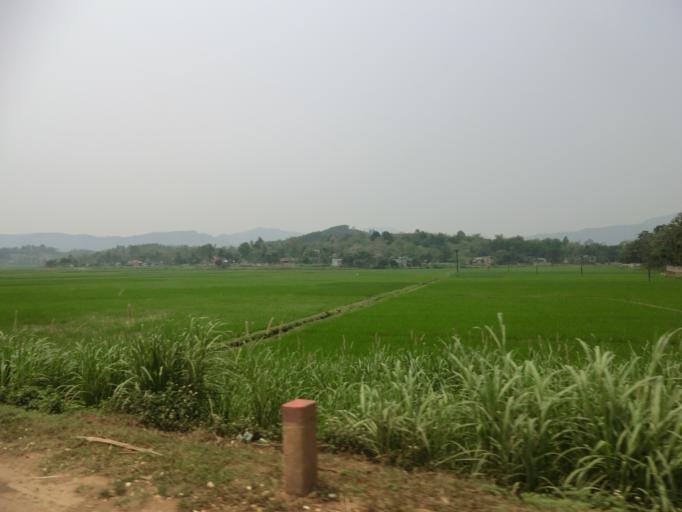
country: VN
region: Thanh Hoa
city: Thi Tran Ngoc Lac
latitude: 20.0347
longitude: 105.4060
